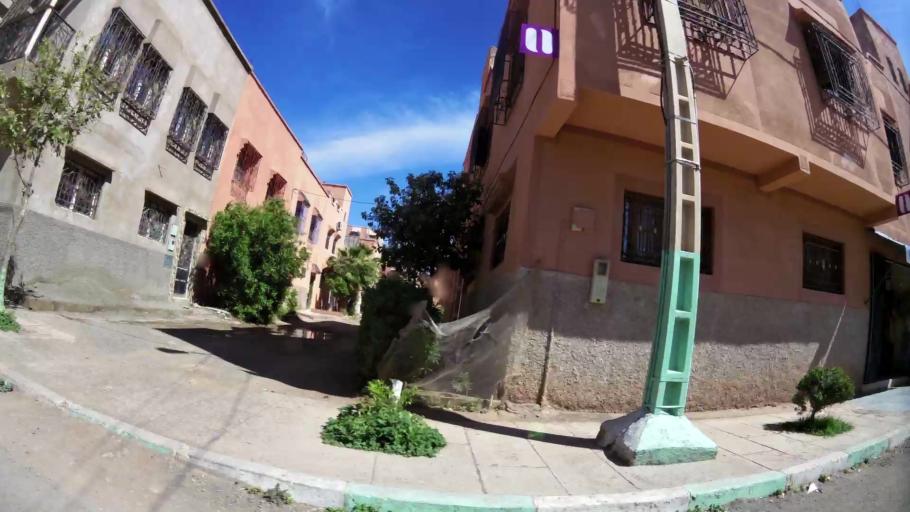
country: MA
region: Marrakech-Tensift-Al Haouz
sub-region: Marrakech
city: Marrakesh
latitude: 31.6438
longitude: -8.1155
